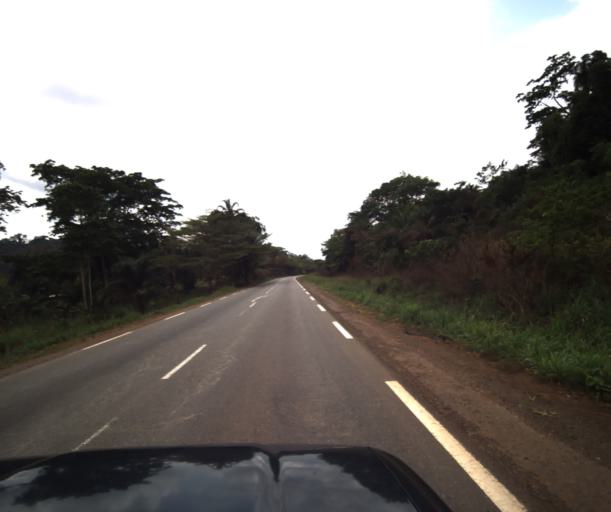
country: CM
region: Centre
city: Eseka
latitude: 3.8343
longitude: 10.9911
